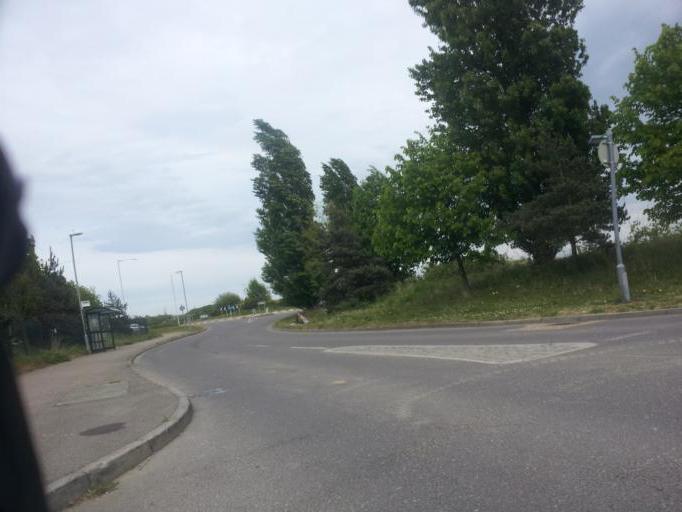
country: GB
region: England
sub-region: Kent
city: Sittingbourne
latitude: 51.3442
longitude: 0.7649
